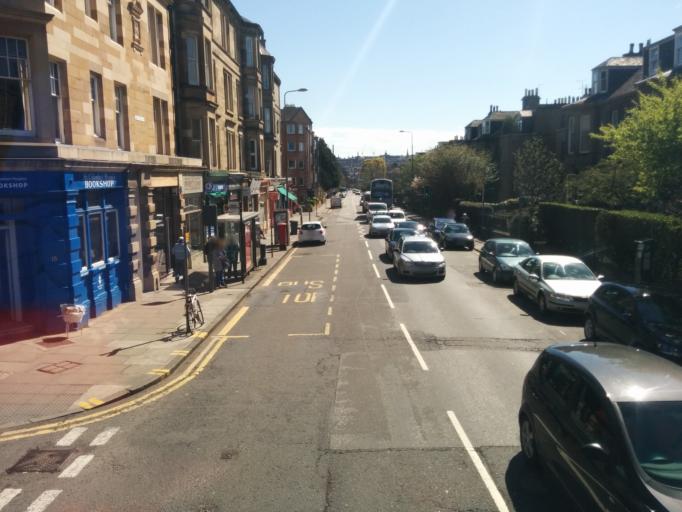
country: GB
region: Scotland
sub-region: Edinburgh
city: Edinburgh
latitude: 55.9703
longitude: -3.2082
